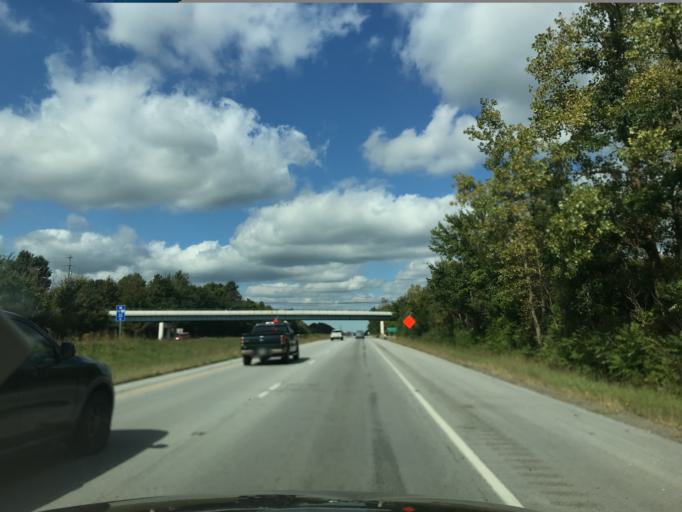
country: US
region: Ohio
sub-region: Summit County
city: Macedonia
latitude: 41.3382
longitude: -81.4871
